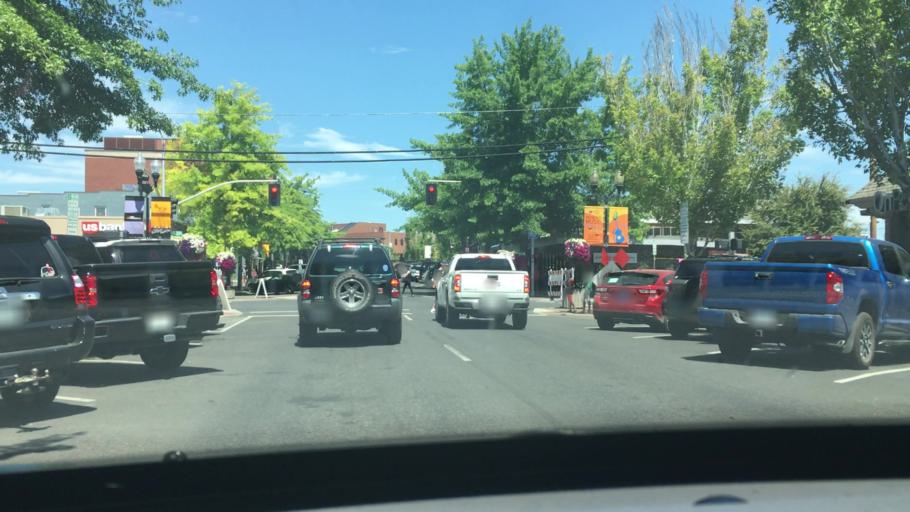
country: US
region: Oregon
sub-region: Deschutes County
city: Bend
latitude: 44.0587
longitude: -121.3126
